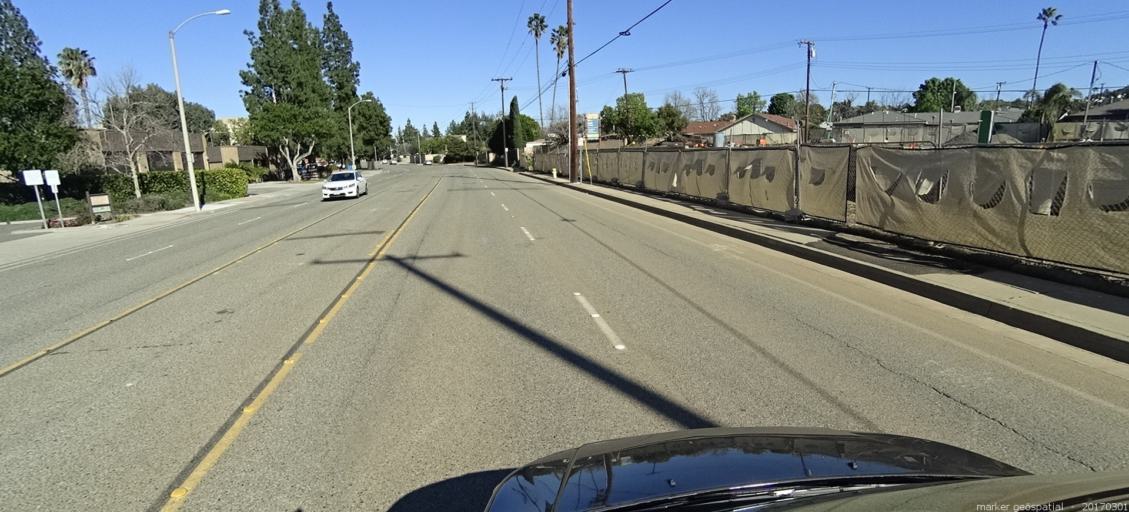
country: US
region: California
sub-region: Orange County
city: Yorba Linda
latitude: 33.8516
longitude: -117.8189
